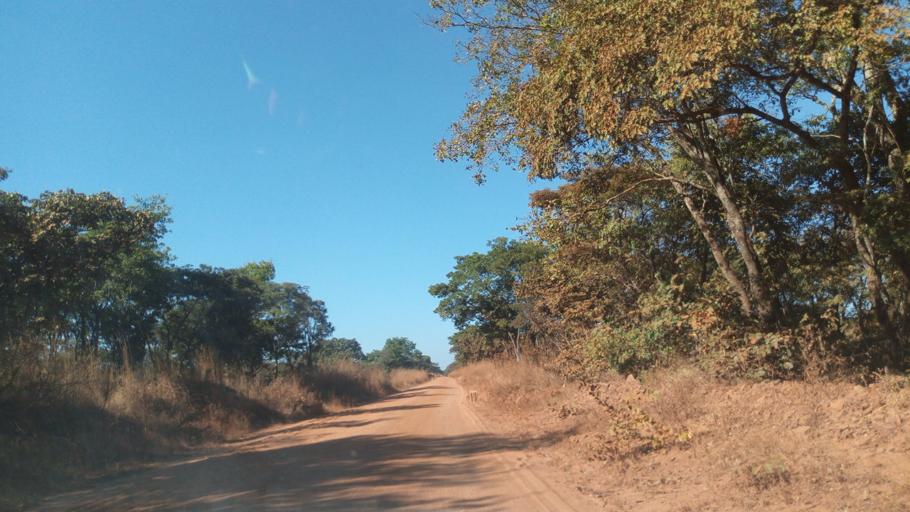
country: ZM
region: Luapula
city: Mwense
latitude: -10.6377
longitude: 28.4092
